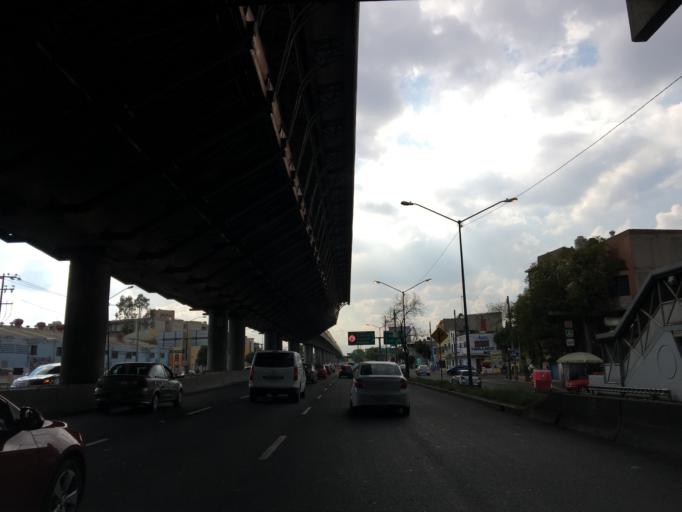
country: MX
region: Mexico City
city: Venustiano Carranza
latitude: 19.4409
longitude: -99.0943
